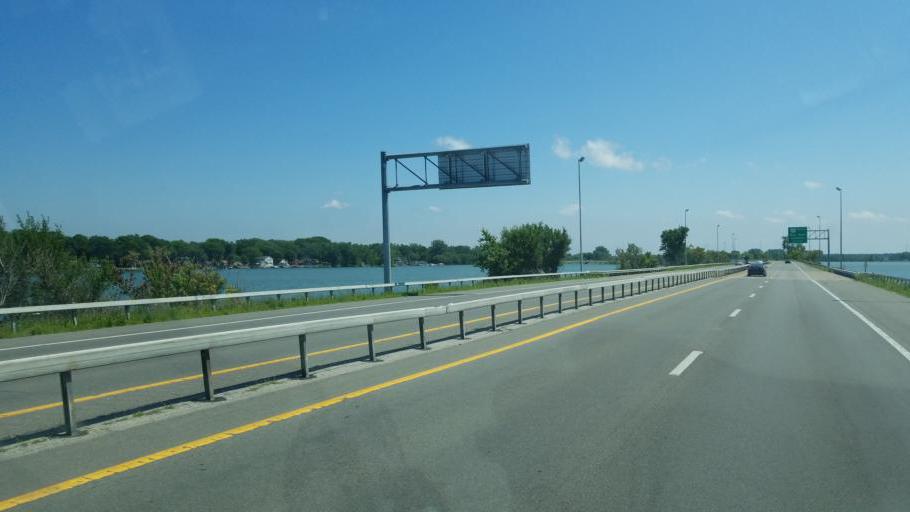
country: US
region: Ohio
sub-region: Ottawa County
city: Port Clinton
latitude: 41.4710
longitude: -82.8334
